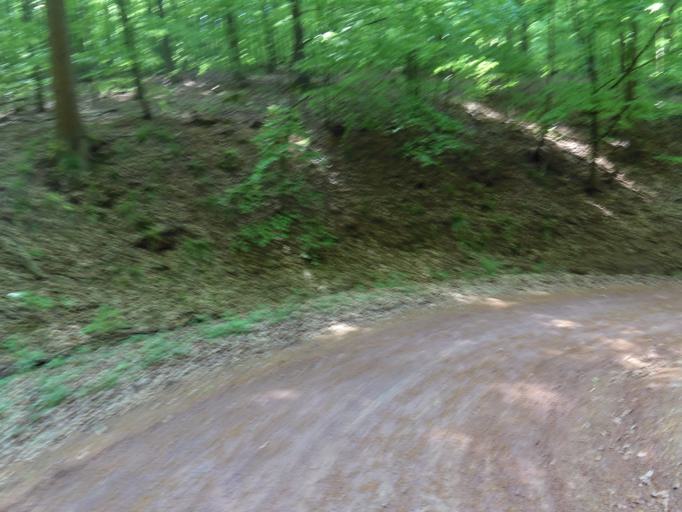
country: DE
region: Thuringia
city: Eisenach
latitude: 50.9550
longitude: 10.2985
